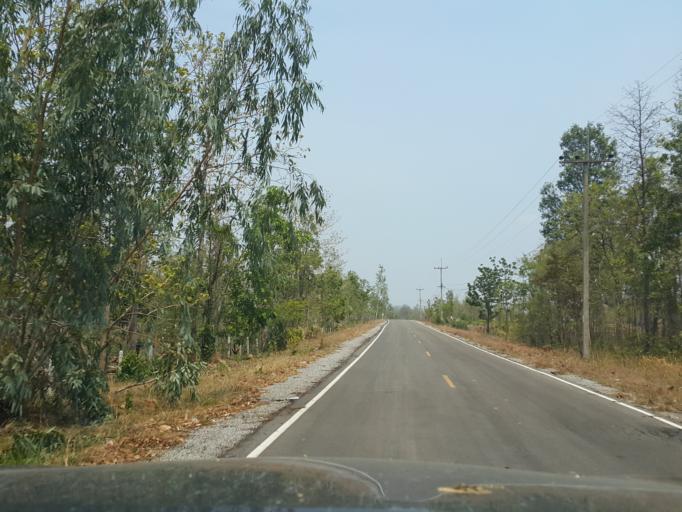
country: TH
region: Lampang
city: Mae Phrik
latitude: 17.5622
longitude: 99.0958
